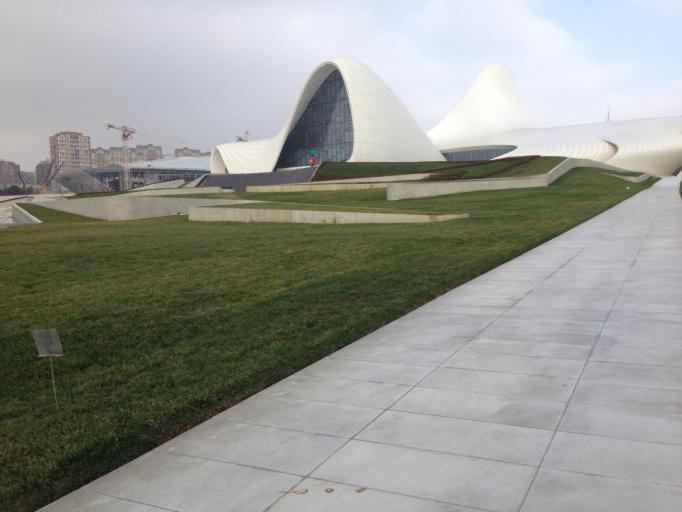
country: AZ
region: Baki
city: Baku
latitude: 40.3936
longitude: 49.8675
